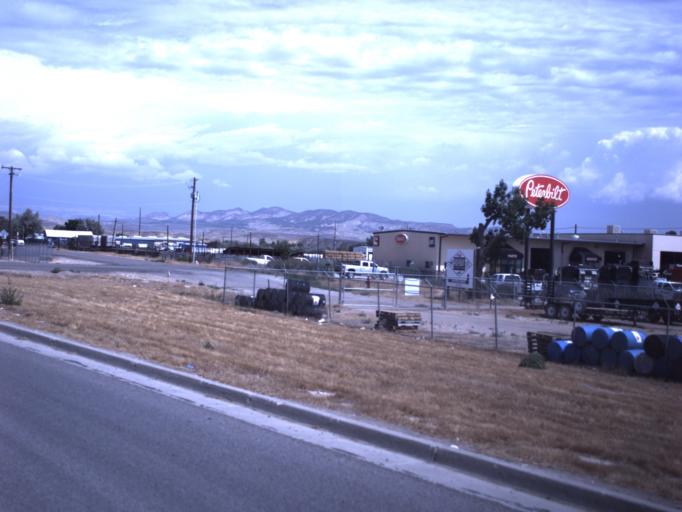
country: US
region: Utah
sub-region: Uintah County
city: Naples
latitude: 40.4452
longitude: -109.5000
